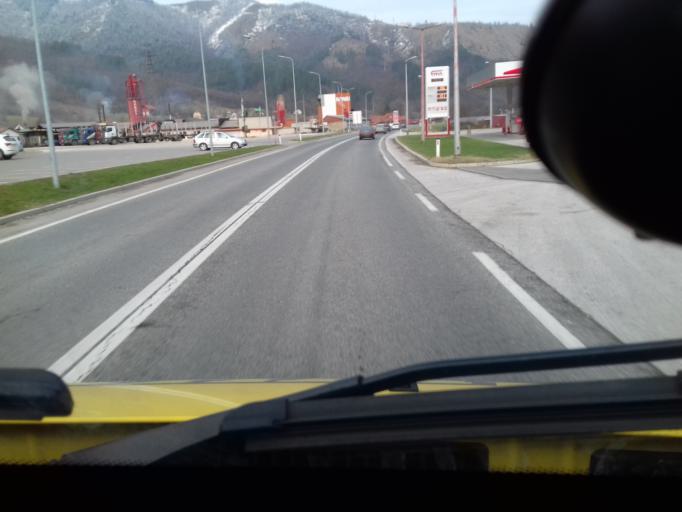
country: BA
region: Federation of Bosnia and Herzegovina
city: Zeljezno Polje
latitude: 44.3915
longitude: 17.9847
